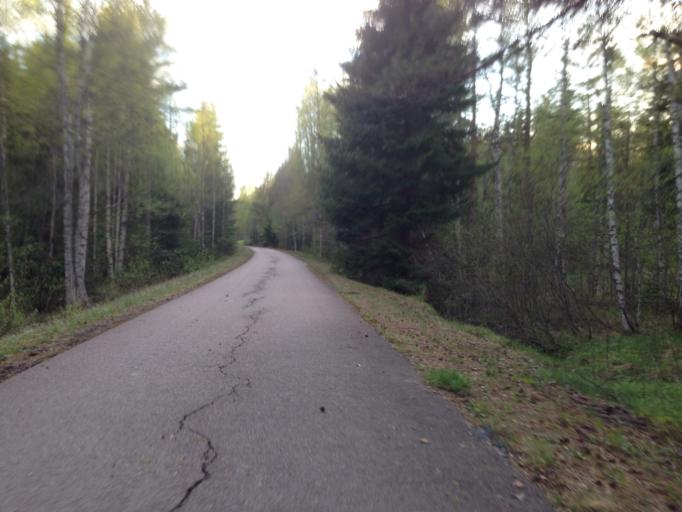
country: SE
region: Dalarna
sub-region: Ludvika Kommun
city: Ludvika
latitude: 60.1415
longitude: 15.0979
